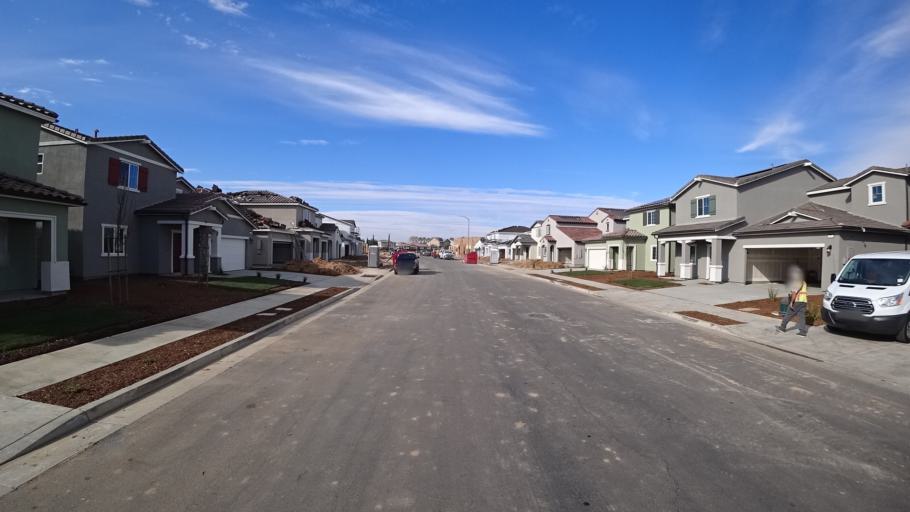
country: US
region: California
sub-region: Kern County
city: Oildale
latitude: 35.4065
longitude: -118.8800
